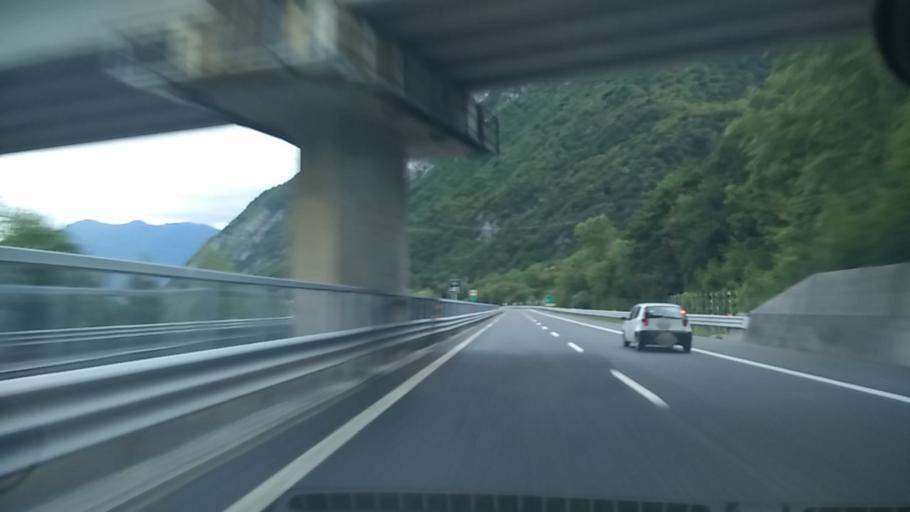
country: IT
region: Friuli Venezia Giulia
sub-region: Provincia di Udine
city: Amaro
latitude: 46.3910
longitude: 13.1380
